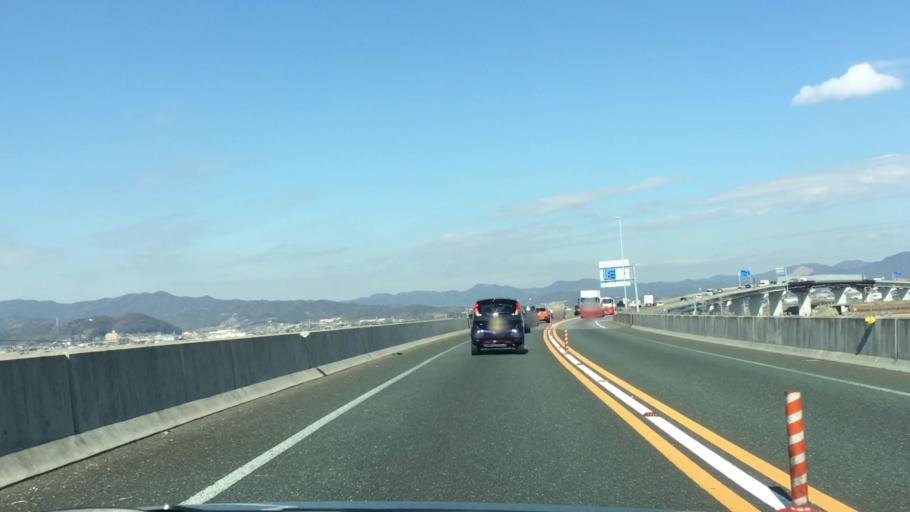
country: JP
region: Aichi
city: Kozakai-cho
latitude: 34.7922
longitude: 137.3310
